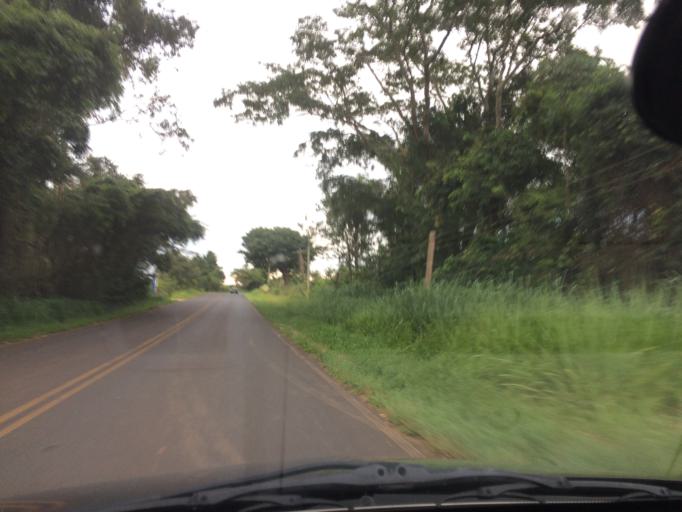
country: BR
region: Sao Paulo
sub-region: Casa Branca
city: Casa Branca
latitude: -21.7655
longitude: -47.1022
